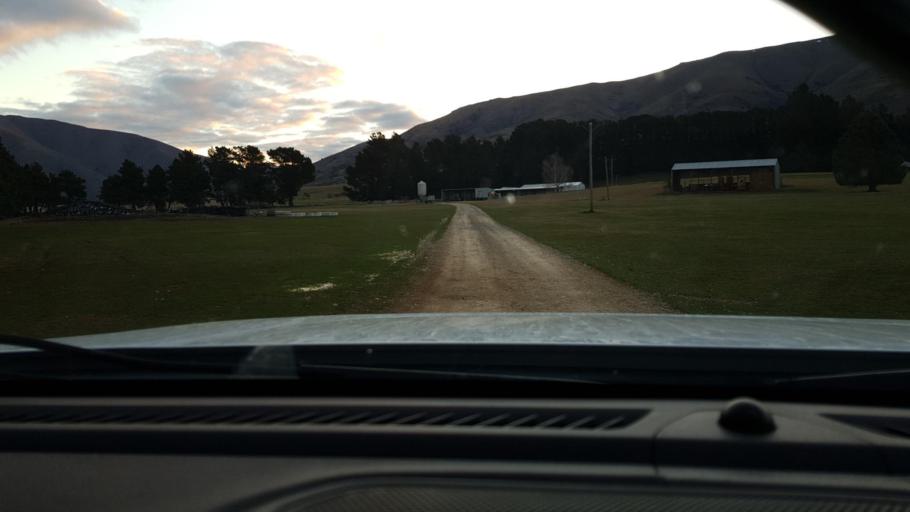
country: NZ
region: Otago
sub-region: Queenstown-Lakes District
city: Wanaka
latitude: -44.4843
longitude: 169.8378
